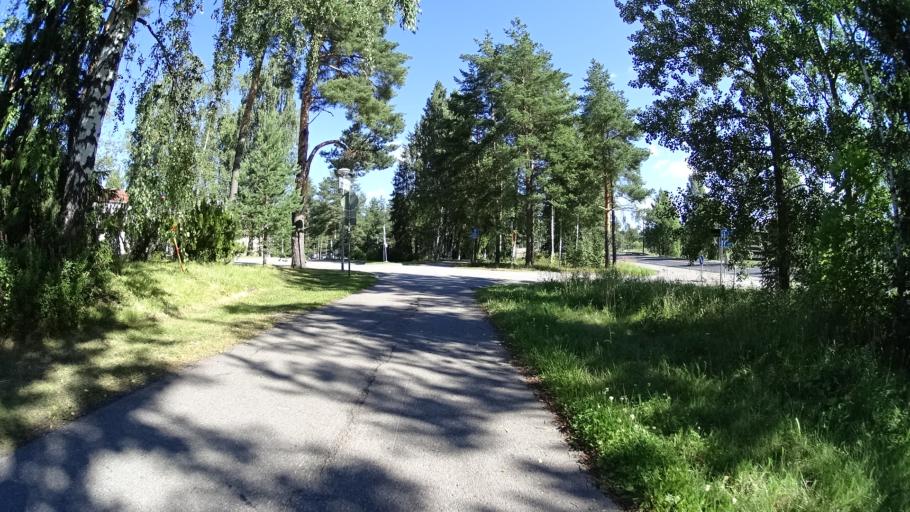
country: FI
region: Uusimaa
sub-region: Helsinki
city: Jaervenpaeae
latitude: 60.4528
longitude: 25.0808
